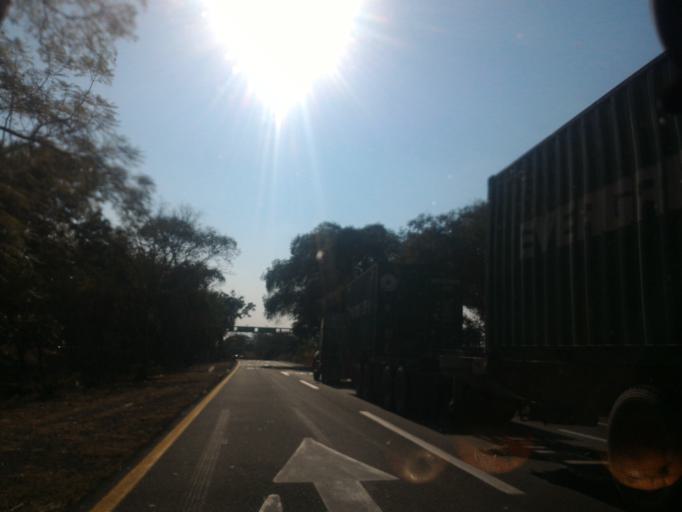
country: MX
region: Colima
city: Colima
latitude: 19.2677
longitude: -103.6780
